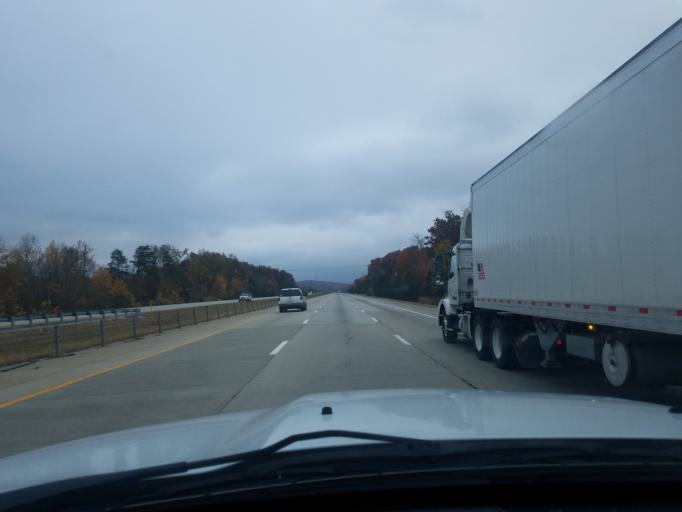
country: US
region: Kentucky
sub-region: Bullitt County
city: Lebanon Junction
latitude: 37.8692
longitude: -85.7047
